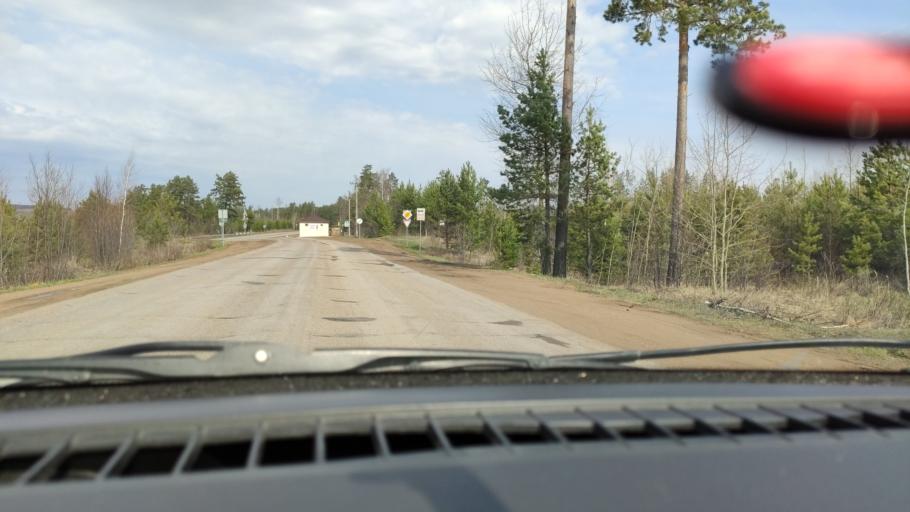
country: RU
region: Bashkortostan
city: Dyurtyuli
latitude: 55.5396
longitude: 54.8613
